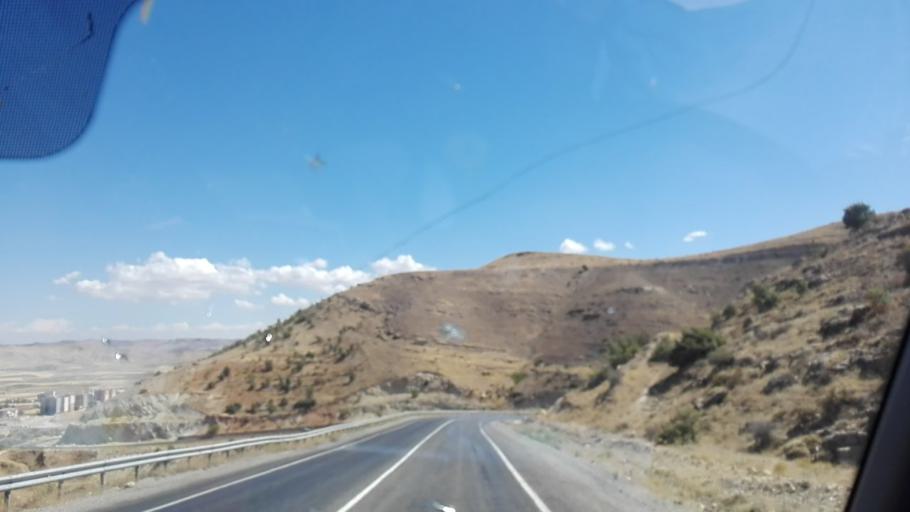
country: TR
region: Batman
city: Gerdzhyush
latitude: 37.5629
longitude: 41.3648
